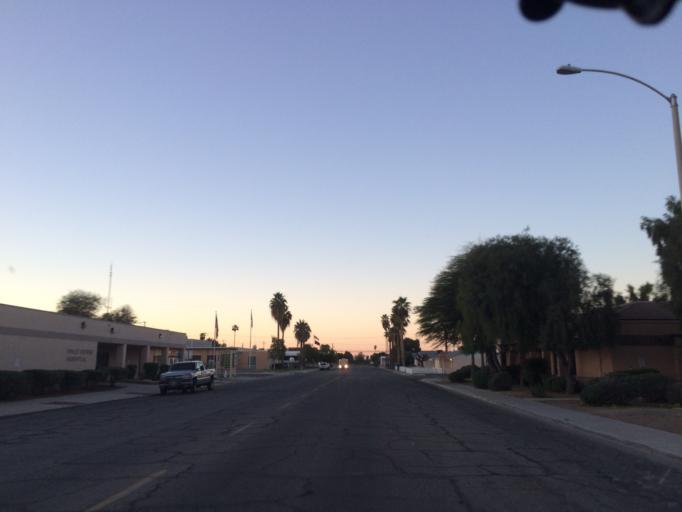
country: US
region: California
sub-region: Riverside County
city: Blythe
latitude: 33.6130
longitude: -114.5955
